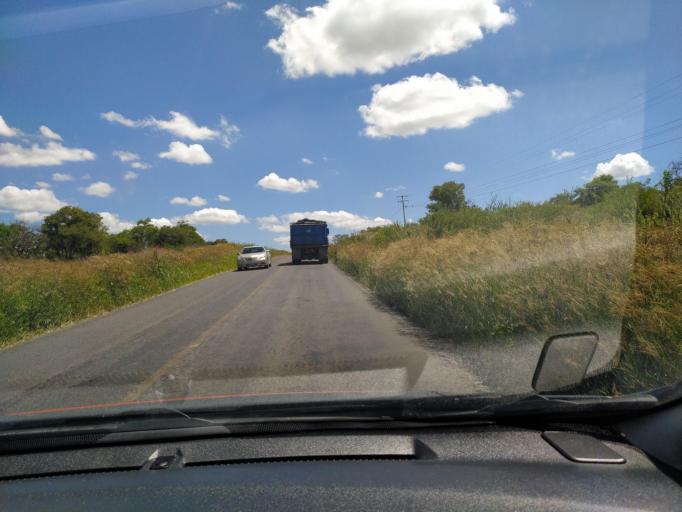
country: MX
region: Jalisco
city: San Diego de Alejandria
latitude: 21.0076
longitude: -102.0245
